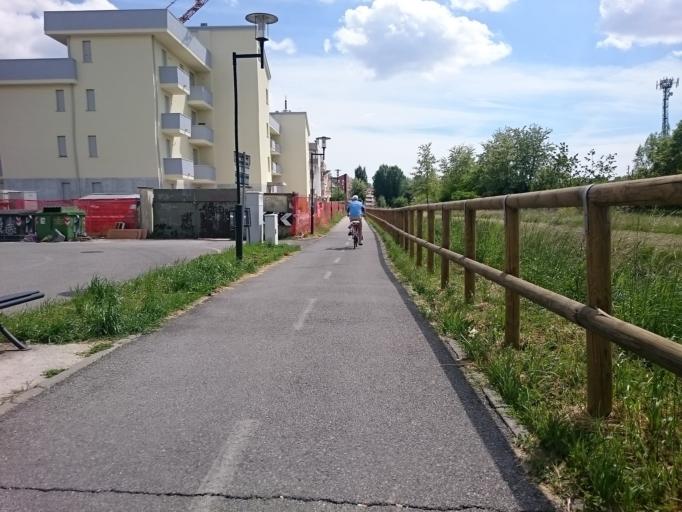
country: IT
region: Veneto
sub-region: Provincia di Rovigo
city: Rovigo
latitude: 45.0814
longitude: 11.7822
